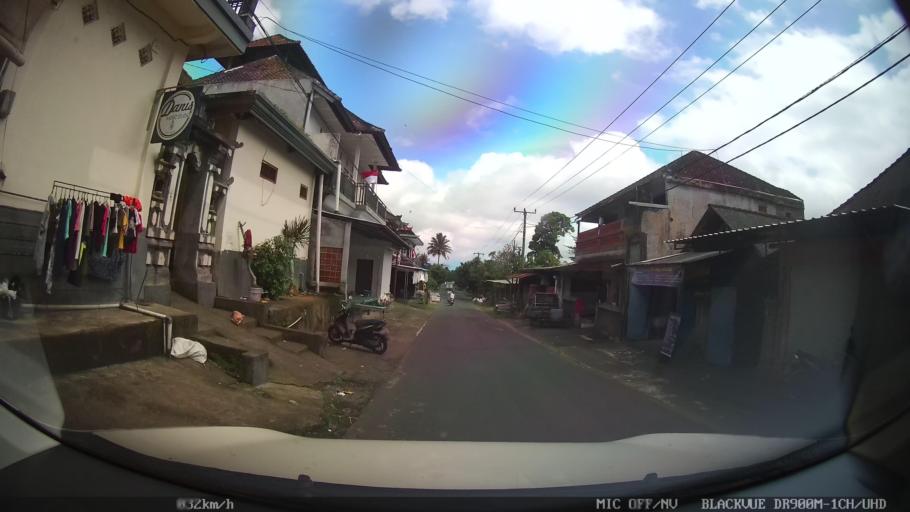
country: ID
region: Bali
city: Banjar Petak
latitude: -8.4513
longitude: 115.3185
